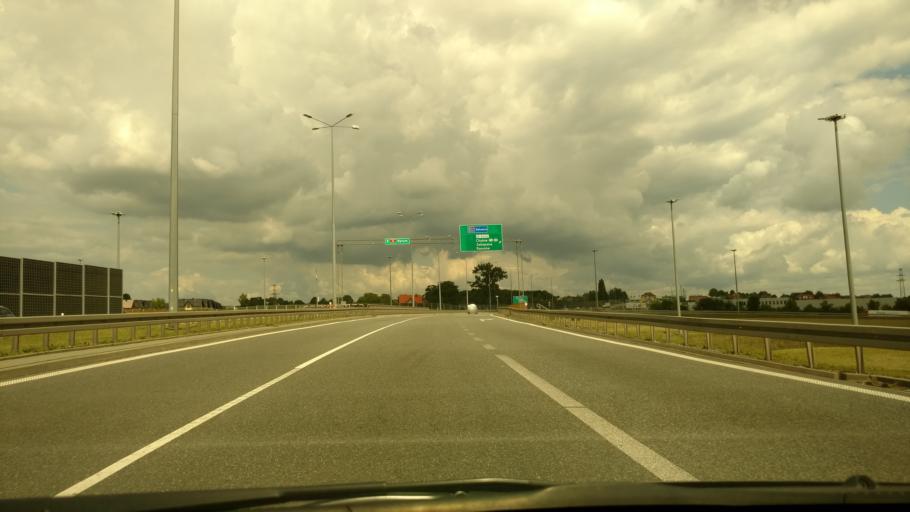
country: PL
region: Lesser Poland Voivodeship
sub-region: Powiat krakowski
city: Modlnica
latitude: 50.1182
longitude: 19.8688
